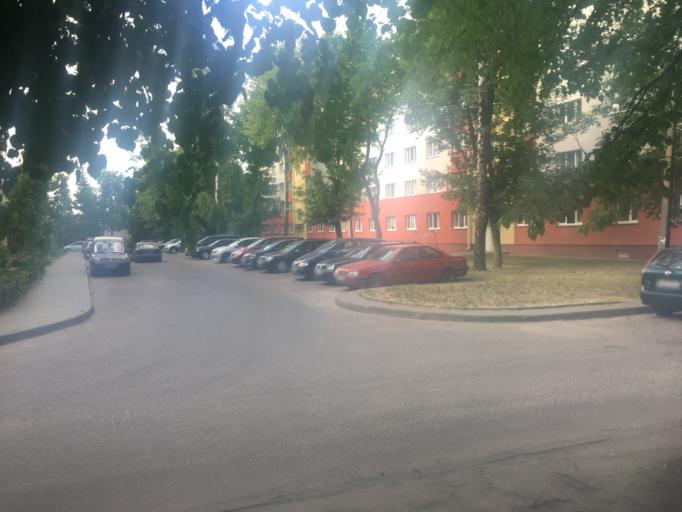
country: BY
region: Grodnenskaya
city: Hrodna
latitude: 53.7068
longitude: 23.8092
